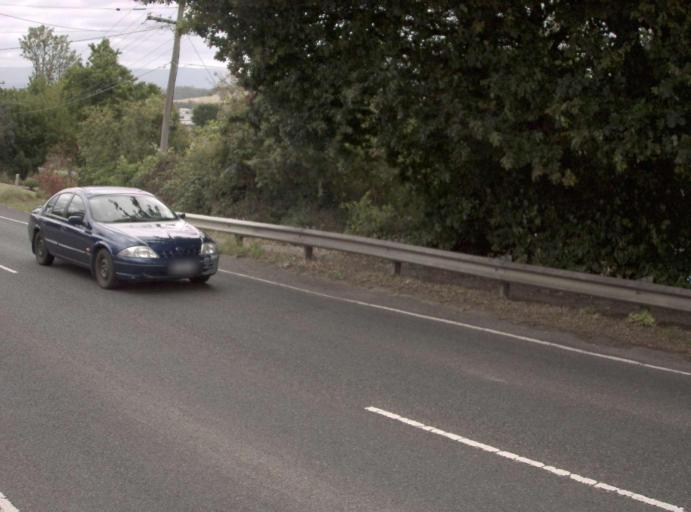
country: AU
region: Victoria
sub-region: Yarra Ranges
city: Lilydale
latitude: -37.7590
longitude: 145.3395
